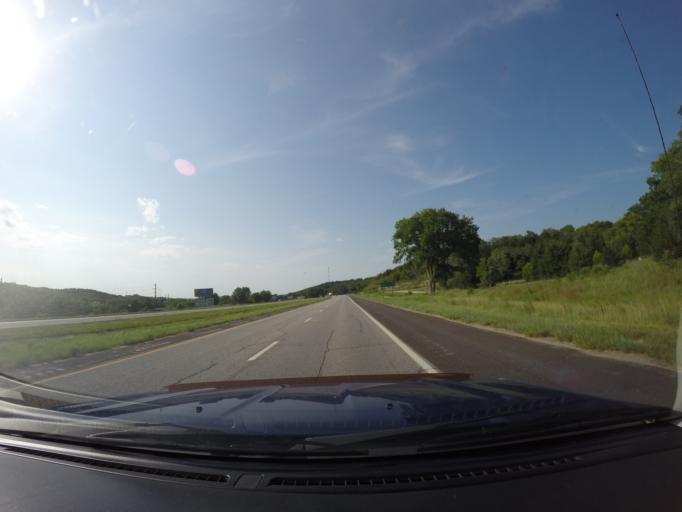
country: US
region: Kansas
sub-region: Riley County
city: Manhattan
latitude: 39.1638
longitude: -96.5397
